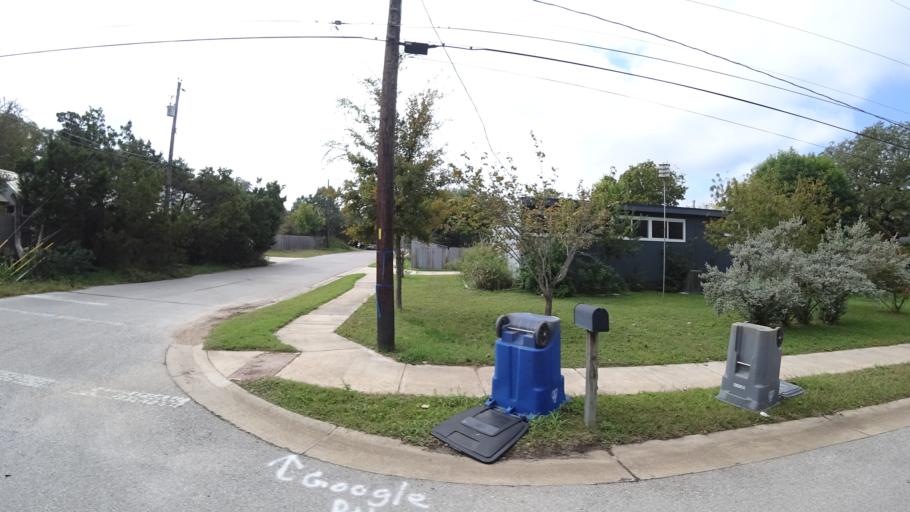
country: US
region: Texas
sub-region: Travis County
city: Shady Hollow
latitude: 30.2051
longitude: -97.8341
